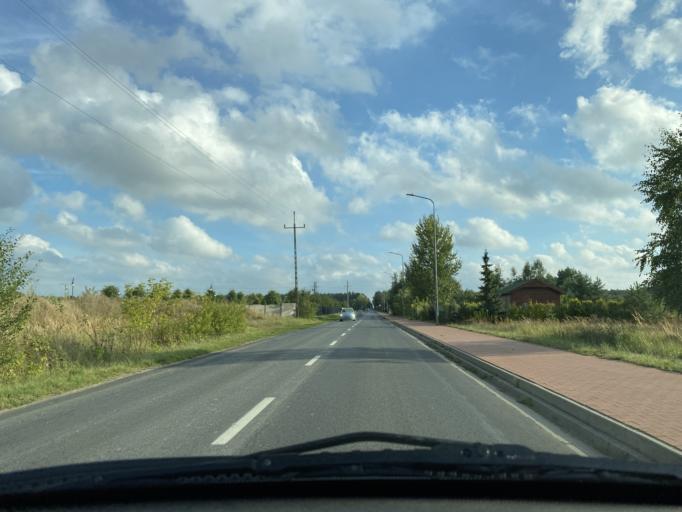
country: PL
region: Greater Poland Voivodeship
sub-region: Powiat poznanski
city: Baranowo
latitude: 52.4175
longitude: 16.7181
